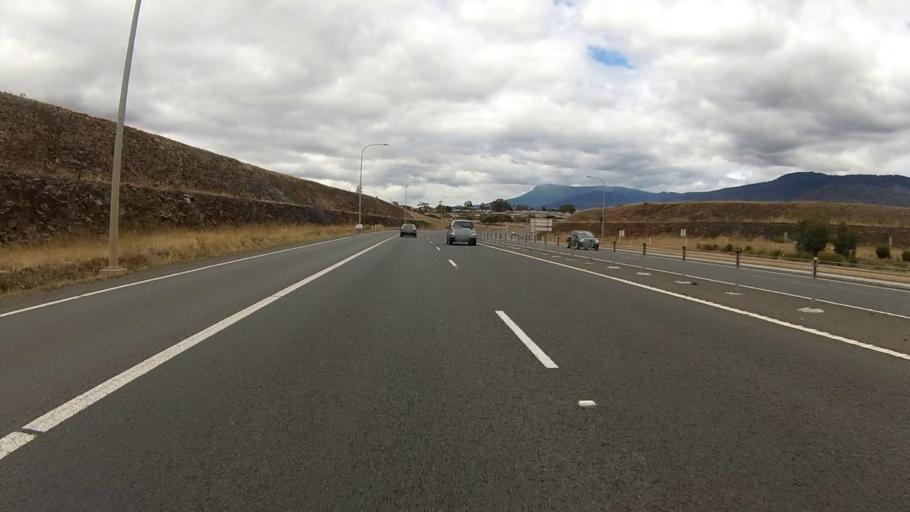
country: AU
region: Tasmania
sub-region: Brighton
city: Bridgewater
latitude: -42.7287
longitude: 147.2375
